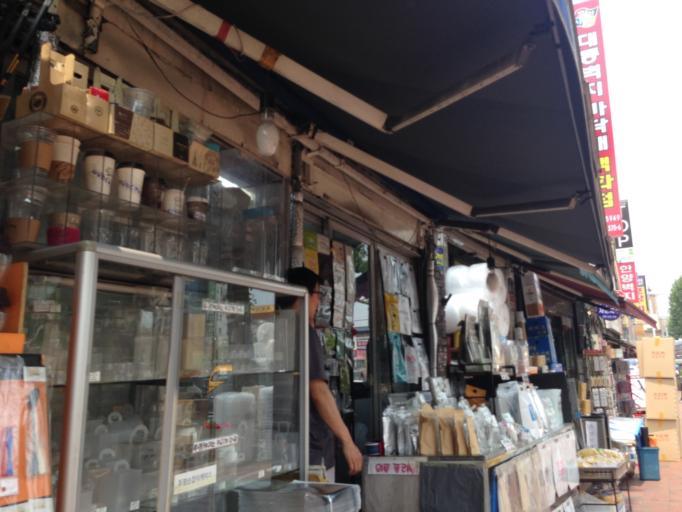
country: KR
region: Seoul
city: Seoul
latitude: 37.5688
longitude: 127.0020
